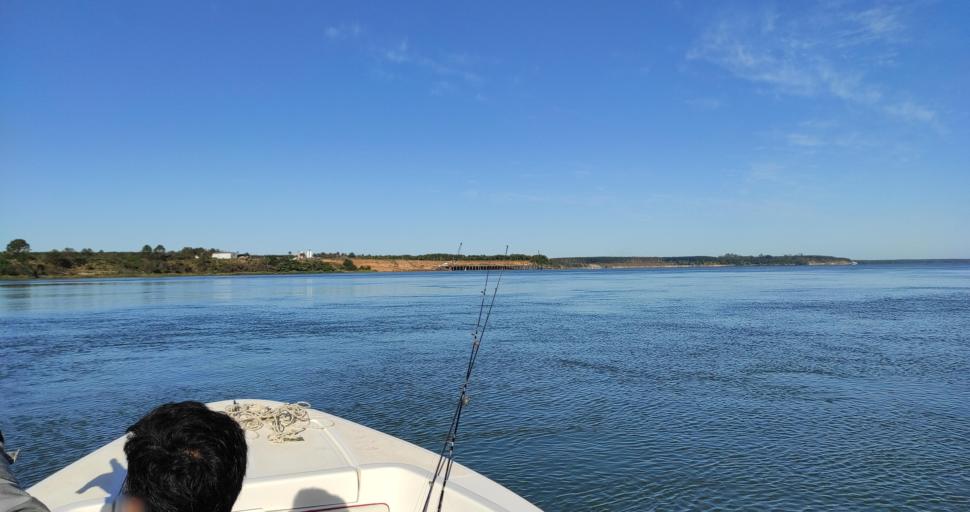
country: AR
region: Corrientes
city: Ituzaingo
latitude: -27.6057
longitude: -56.8268
